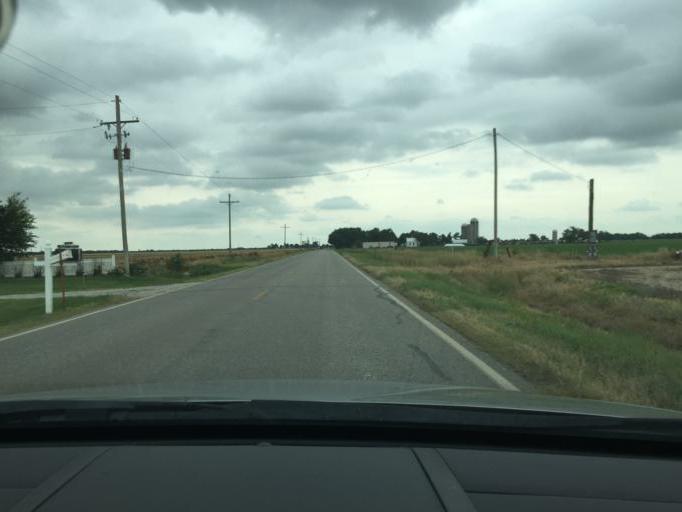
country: US
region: Kansas
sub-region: Reno County
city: South Hutchinson
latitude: 37.9768
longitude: -98.0138
